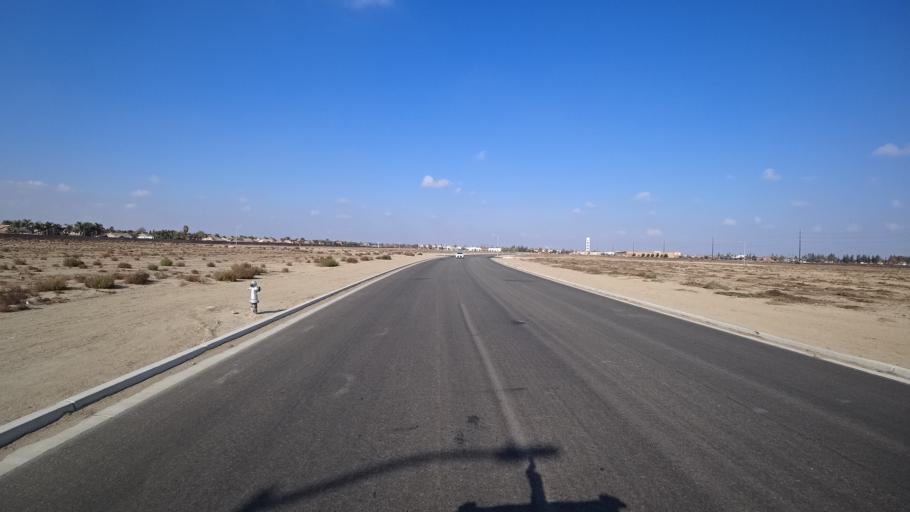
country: US
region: California
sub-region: Kern County
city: Greenacres
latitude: 35.2974
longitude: -119.0988
